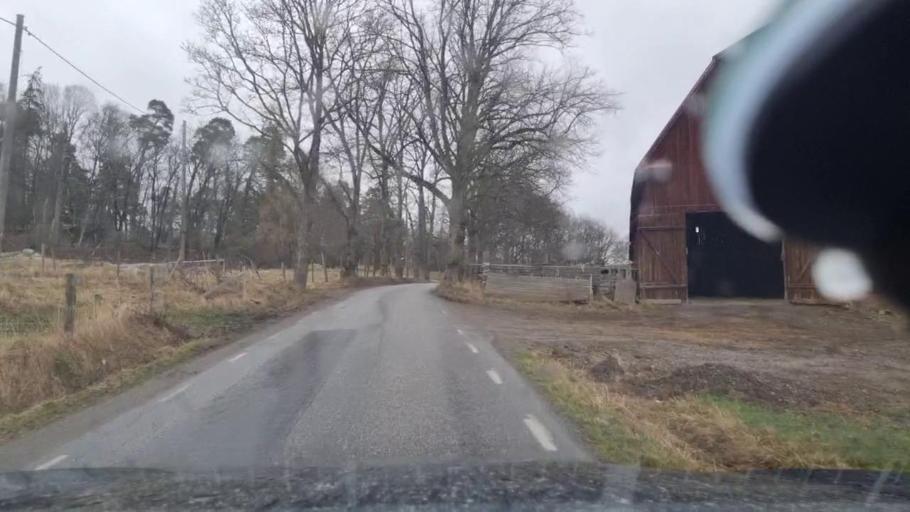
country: SE
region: Stockholm
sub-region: Vallentuna Kommun
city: Vallentuna
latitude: 59.4991
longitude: 18.0079
